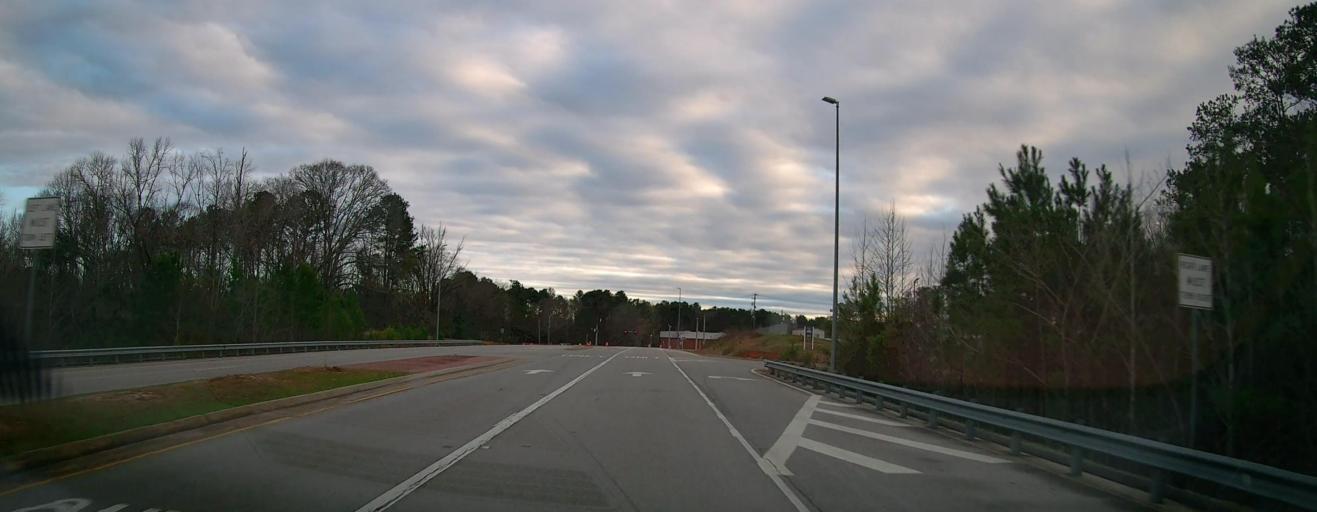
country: US
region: Georgia
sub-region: Troup County
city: West Point
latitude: 32.8812
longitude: -85.1547
